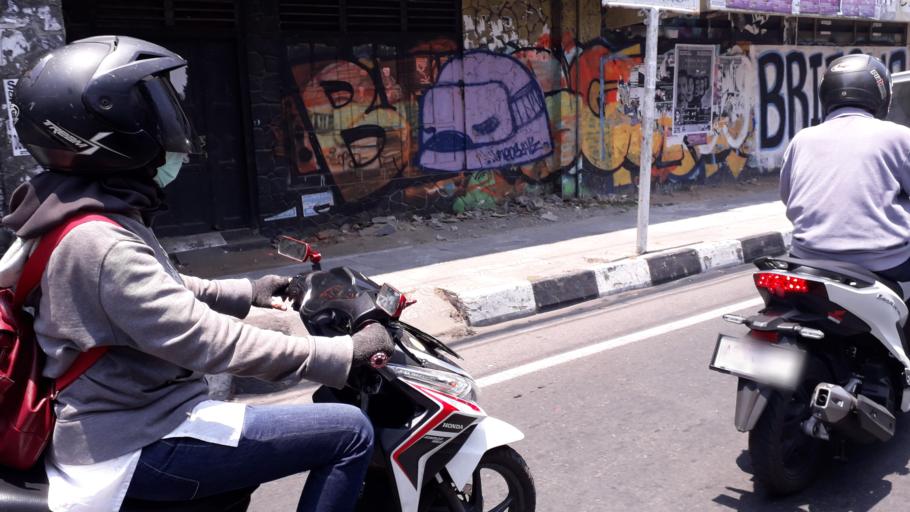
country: ID
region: Daerah Istimewa Yogyakarta
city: Yogyakarta
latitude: -7.7823
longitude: 110.3609
